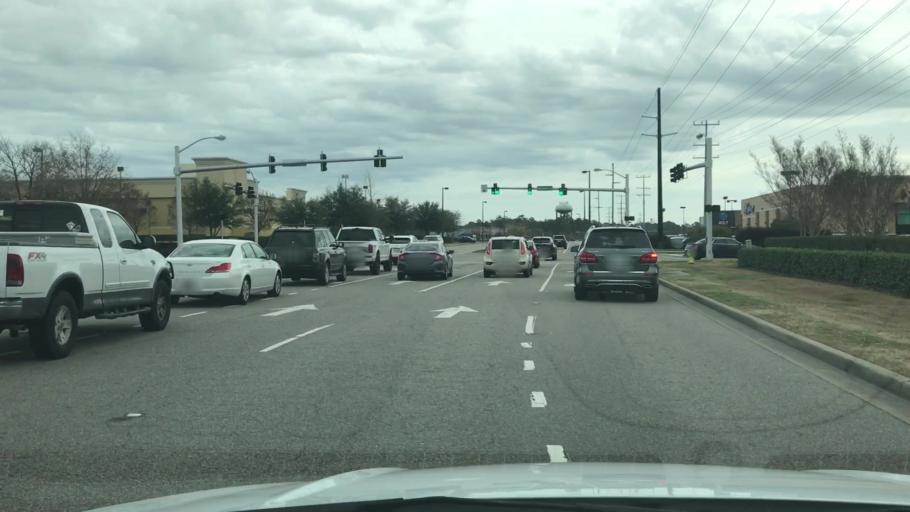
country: US
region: South Carolina
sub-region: Horry County
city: Myrtle Beach
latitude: 33.7061
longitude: -78.9201
